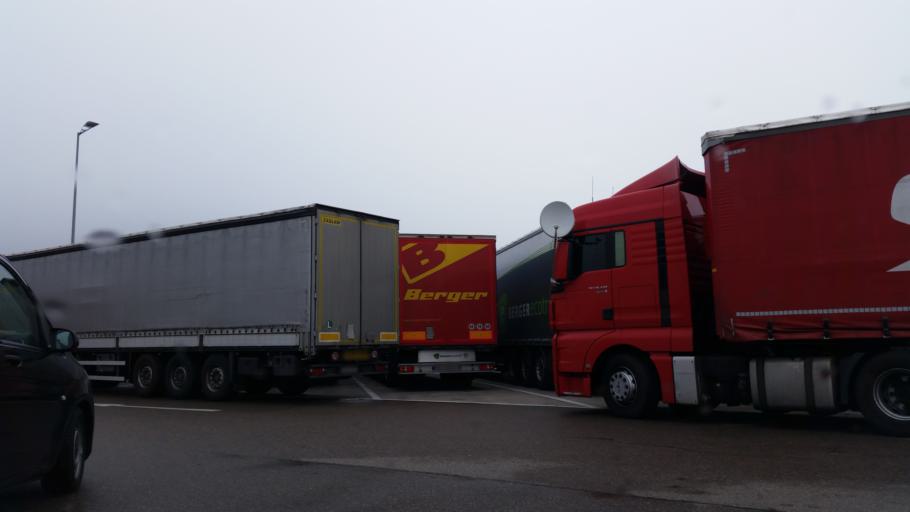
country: DE
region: Bavaria
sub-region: Upper Bavaria
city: Vaterstetten
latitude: 48.1250
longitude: 11.7606
